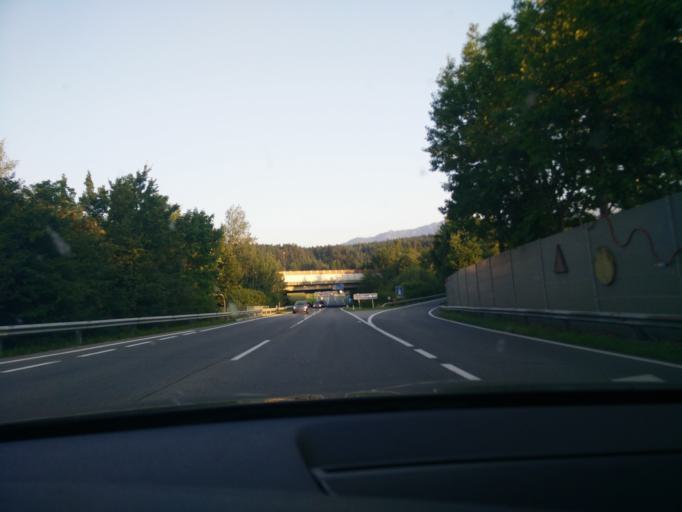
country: AT
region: Carinthia
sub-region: Villach Stadt
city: Villach
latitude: 46.6003
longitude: 13.8827
